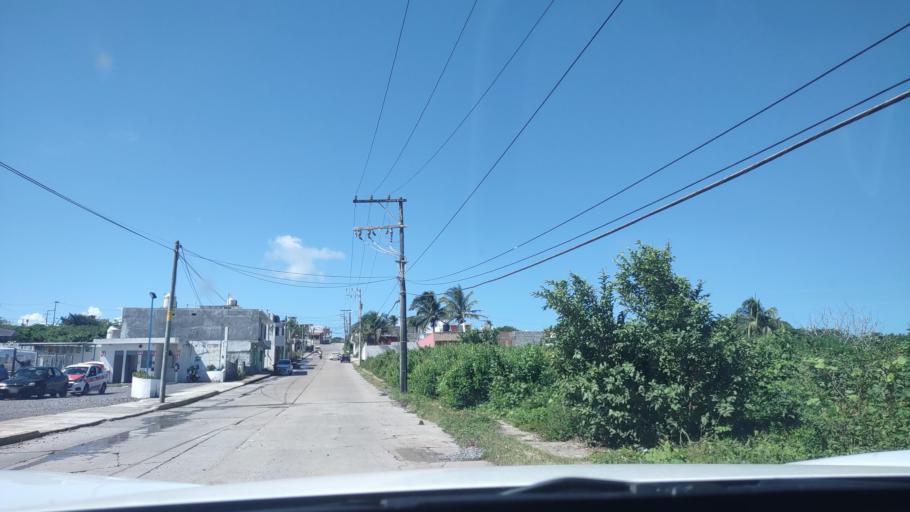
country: MX
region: Veracruz
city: Heroica Alvarado
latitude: 18.7826
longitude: -95.7703
